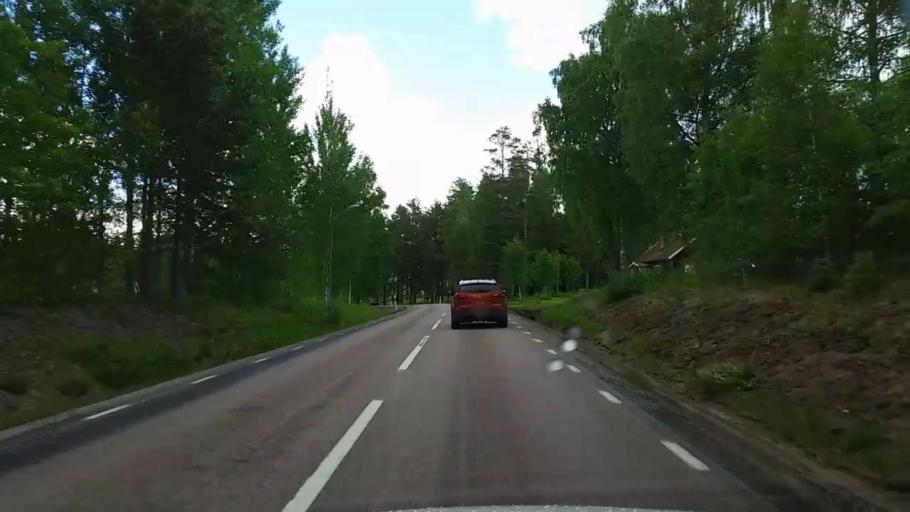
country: SE
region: Vaestmanland
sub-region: Skinnskattebergs Kommun
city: Skinnskatteberg
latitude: 59.8582
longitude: 15.8420
